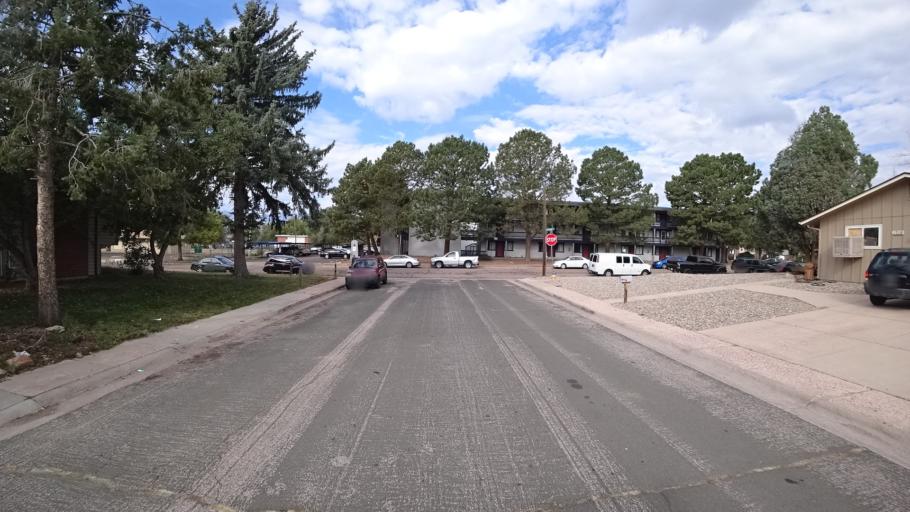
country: US
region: Colorado
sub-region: El Paso County
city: Cimarron Hills
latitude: 38.8515
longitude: -104.7523
